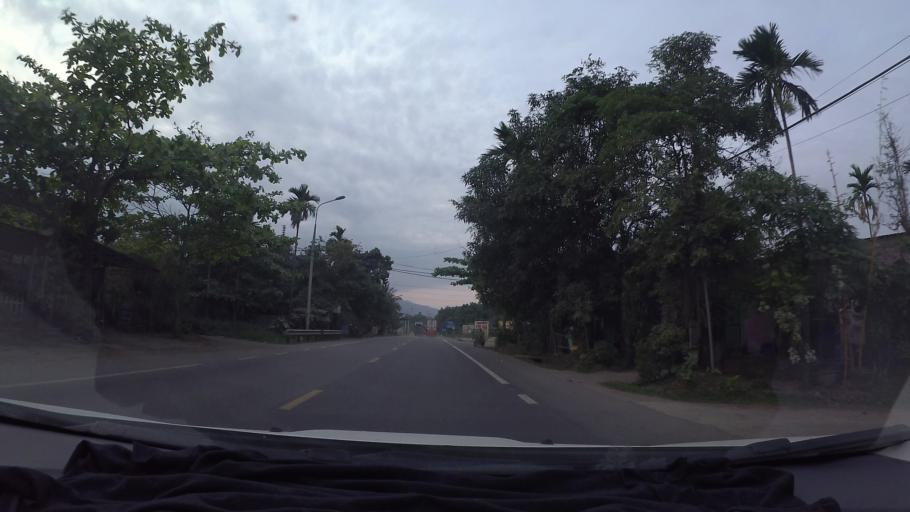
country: VN
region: Da Nang
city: Lien Chieu
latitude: 16.0545
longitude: 108.1023
